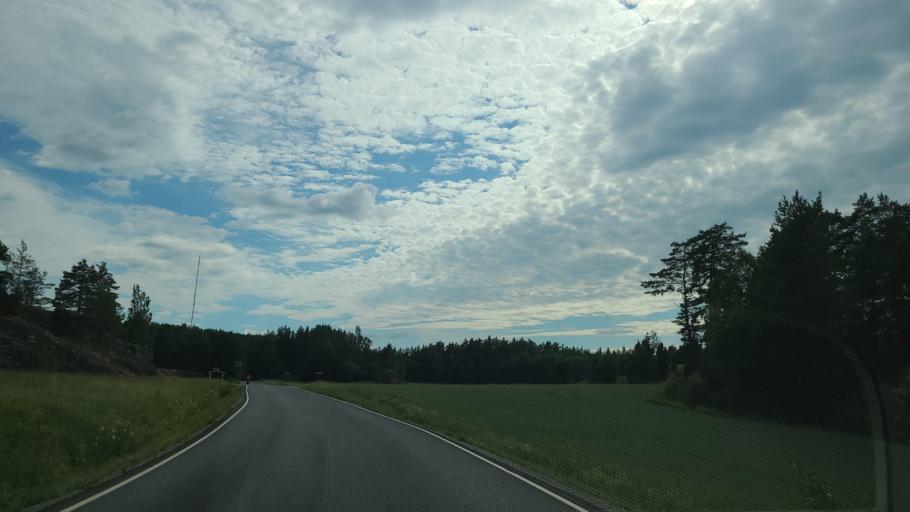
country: FI
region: Varsinais-Suomi
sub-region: Turku
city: Rymaettylae
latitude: 60.3300
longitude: 21.9725
